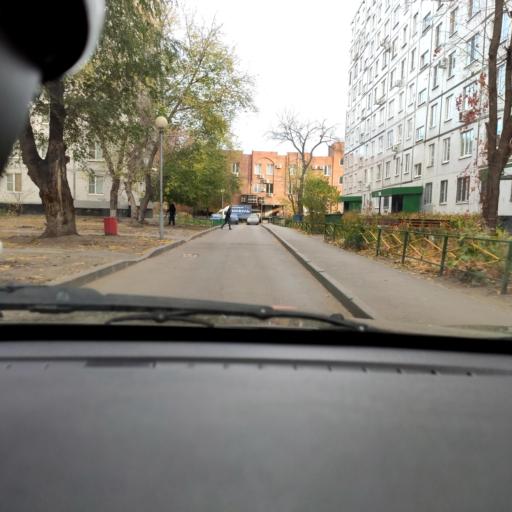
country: RU
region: Samara
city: Tol'yatti
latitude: 53.5148
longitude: 49.2617
